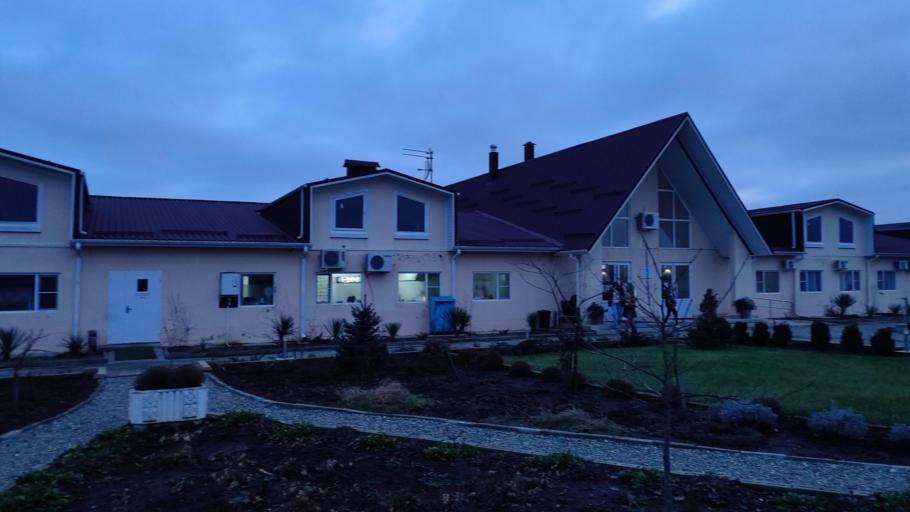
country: RU
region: Krasnodarskiy
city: Yaroslavskaya
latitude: 44.6054
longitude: 40.4433
